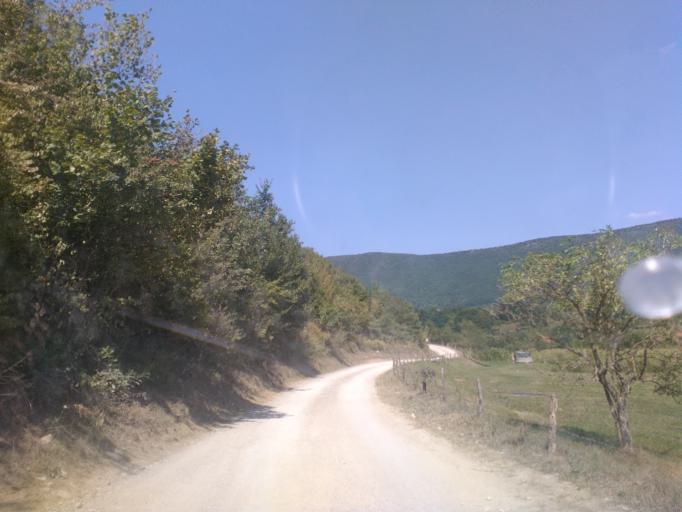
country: BA
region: Federation of Bosnia and Herzegovina
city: Orasac
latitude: 44.6213
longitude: 16.0632
